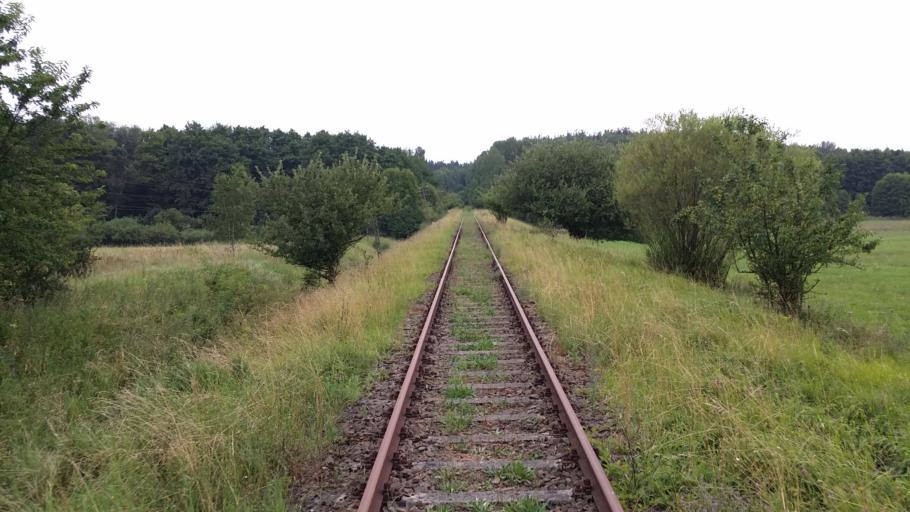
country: PL
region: West Pomeranian Voivodeship
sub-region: Powiat choszczenski
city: Drawno
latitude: 53.2071
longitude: 15.7595
